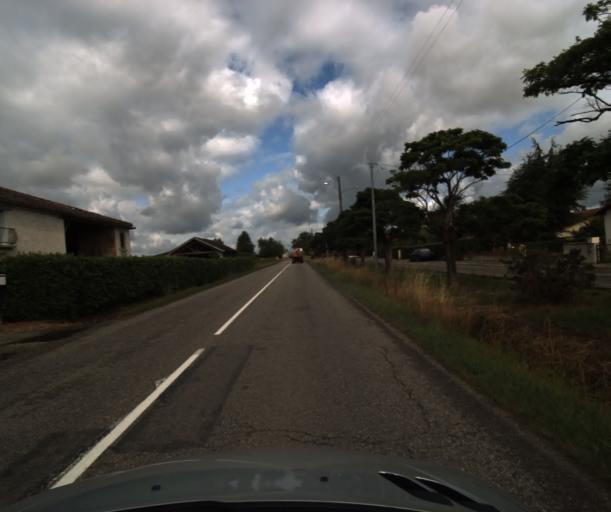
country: FR
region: Midi-Pyrenees
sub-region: Departement du Tarn-et-Garonne
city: Castelsarrasin
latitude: 44.0214
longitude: 1.0669
